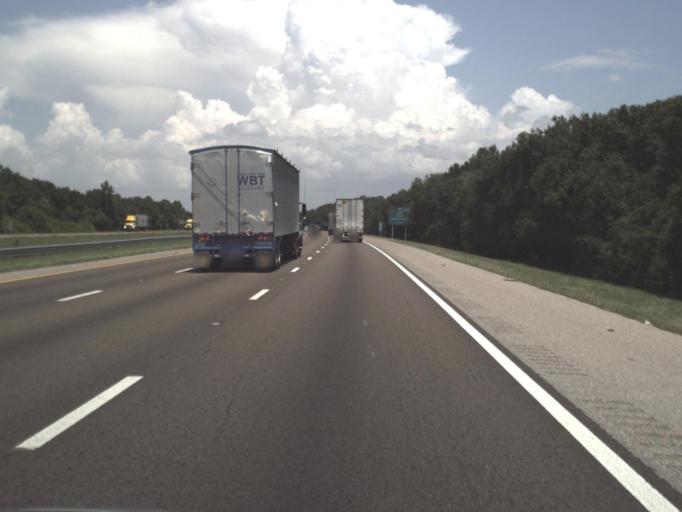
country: US
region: Florida
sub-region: Hillsborough County
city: Apollo Beach
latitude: 27.7700
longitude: -82.3637
